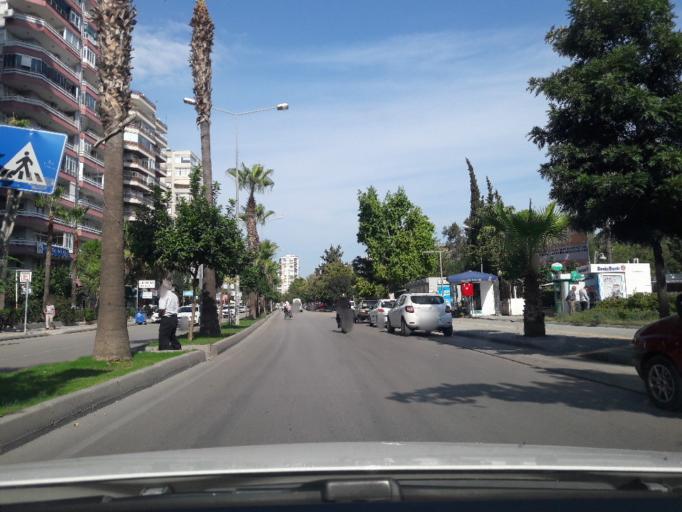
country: TR
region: Adana
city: Adana
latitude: 37.0170
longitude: 35.3218
